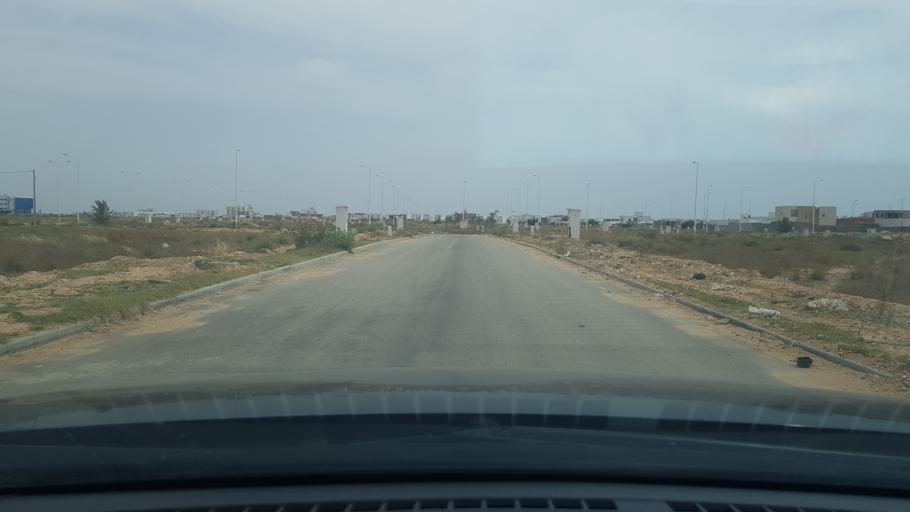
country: TN
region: Safaqis
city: Al Qarmadah
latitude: 34.8264
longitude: 10.7448
